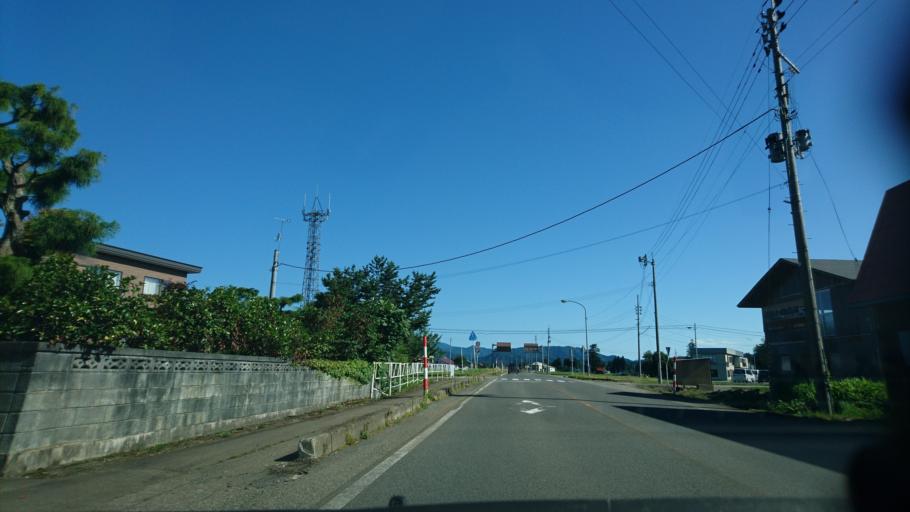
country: JP
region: Akita
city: Kakunodatemachi
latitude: 39.6216
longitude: 140.5720
